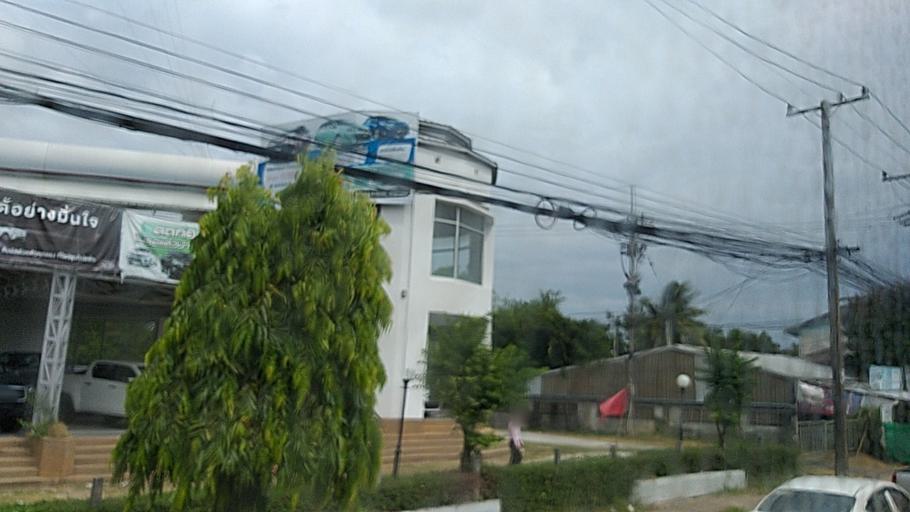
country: TH
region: Roi Et
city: Roi Et
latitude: 16.0570
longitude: 103.6356
